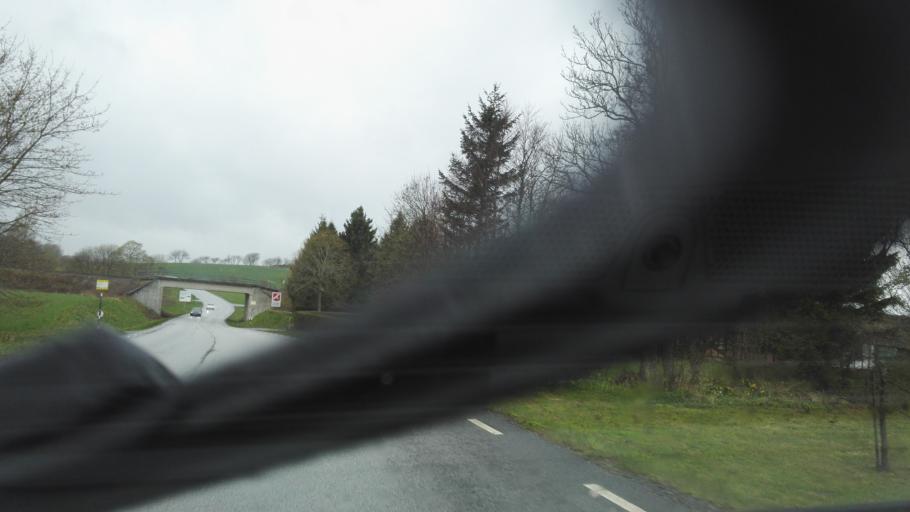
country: SE
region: Skane
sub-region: Simrishamns Kommun
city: Kivik
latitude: 55.7180
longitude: 14.1429
